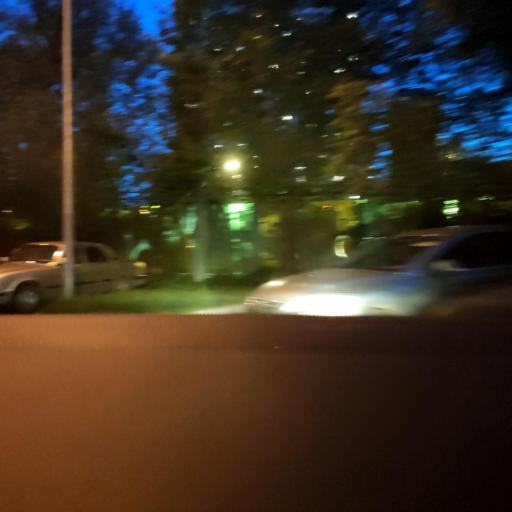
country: RU
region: Moscow
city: Severnyy
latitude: 55.9330
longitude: 37.5541
